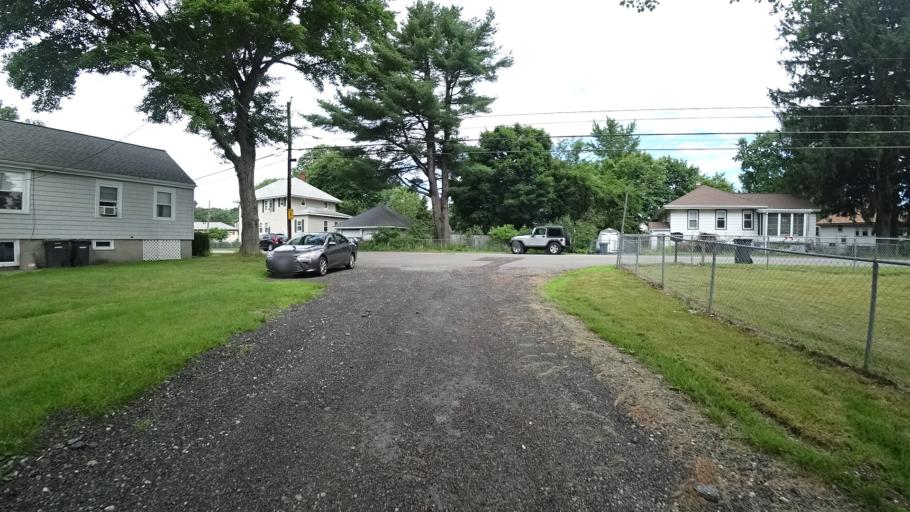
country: US
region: Massachusetts
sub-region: Norfolk County
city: Dedham
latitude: 42.2271
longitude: -71.1427
